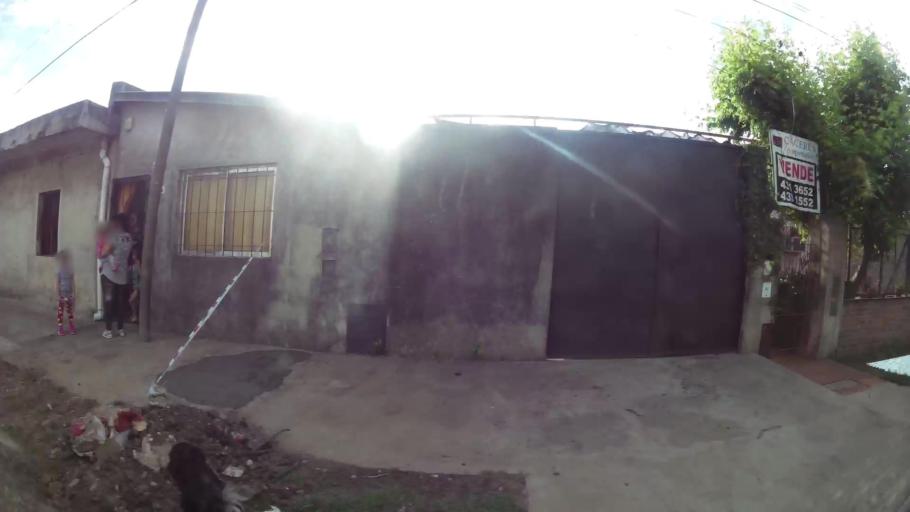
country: AR
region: Santa Fe
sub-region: Departamento de Rosario
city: Rosario
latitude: -32.9810
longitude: -60.6805
